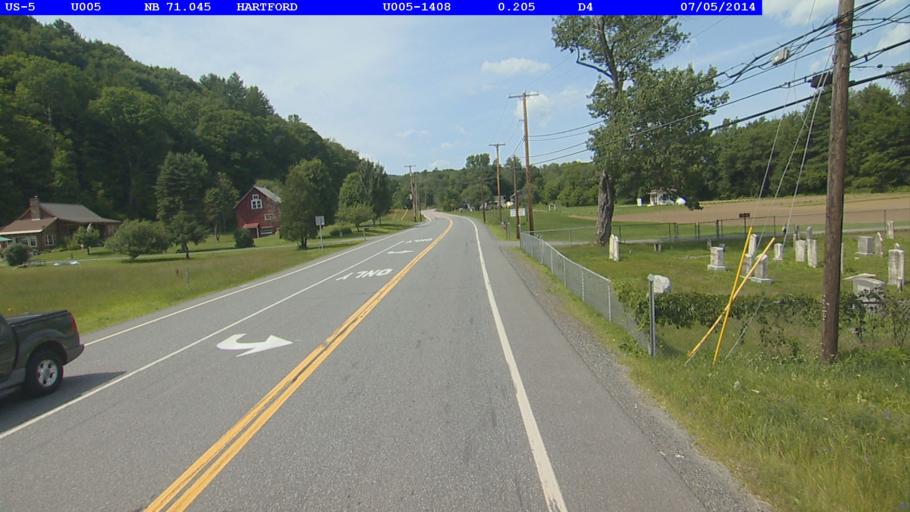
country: US
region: Vermont
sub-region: Windsor County
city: White River Junction
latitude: 43.6137
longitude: -72.3543
